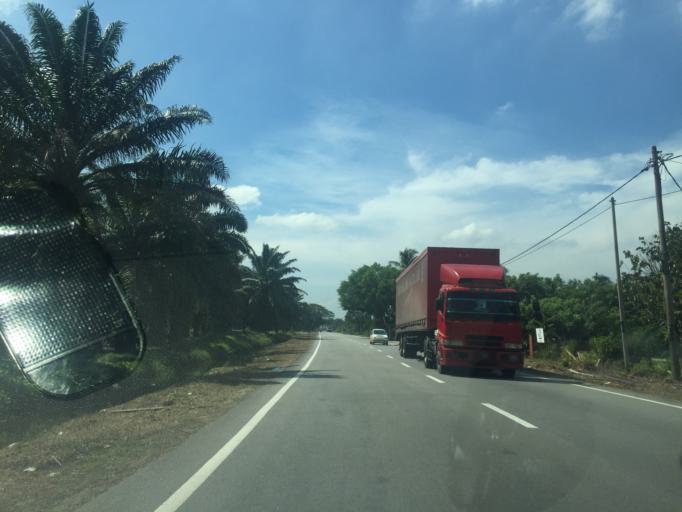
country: MY
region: Penang
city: Tasek Glugor
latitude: 5.4909
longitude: 100.5065
